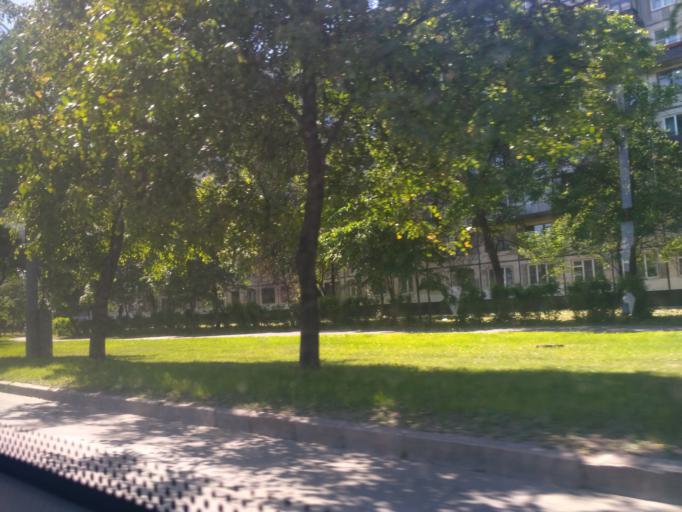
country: RU
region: Leningrad
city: Kalininskiy
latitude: 59.9633
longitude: 30.4210
